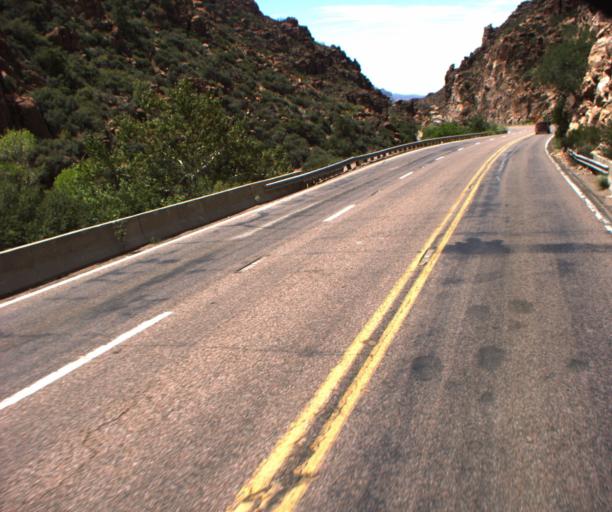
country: US
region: Arizona
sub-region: Pinal County
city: Superior
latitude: 33.3098
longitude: -111.0676
